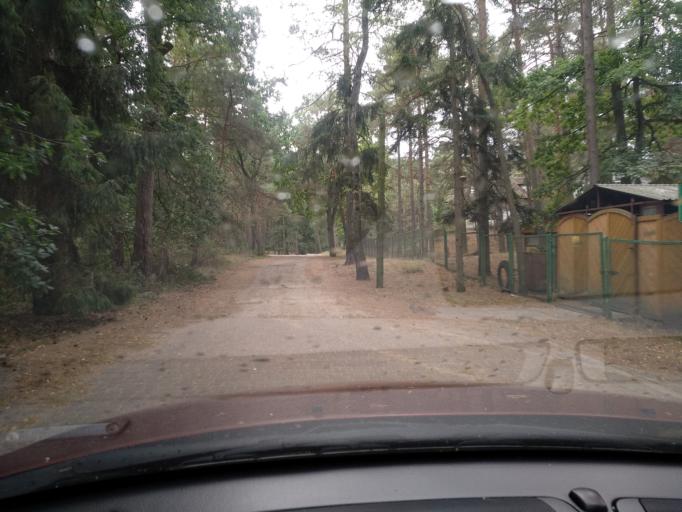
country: PL
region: West Pomeranian Voivodeship
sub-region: Powiat gryficki
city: Pobierowo
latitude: 54.0529
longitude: 14.9248
